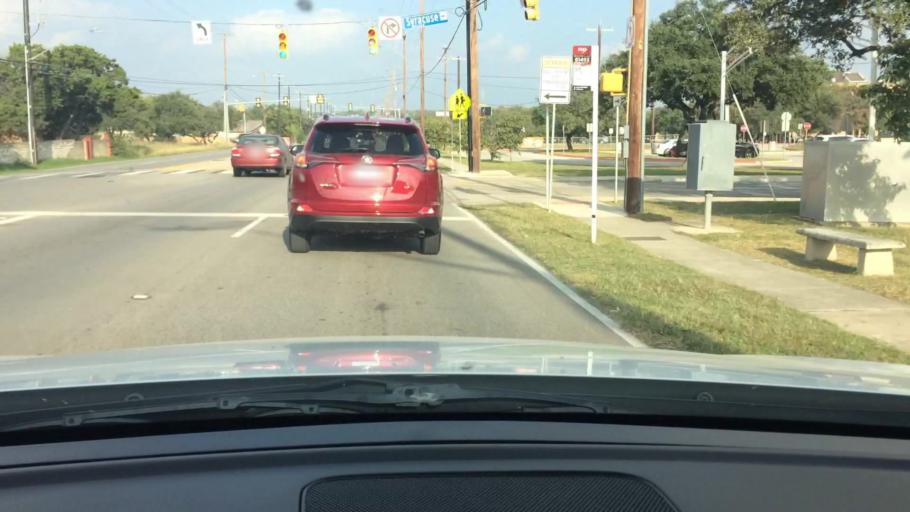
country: US
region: Texas
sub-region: Bexar County
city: Shavano Park
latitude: 29.5659
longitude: -98.5836
